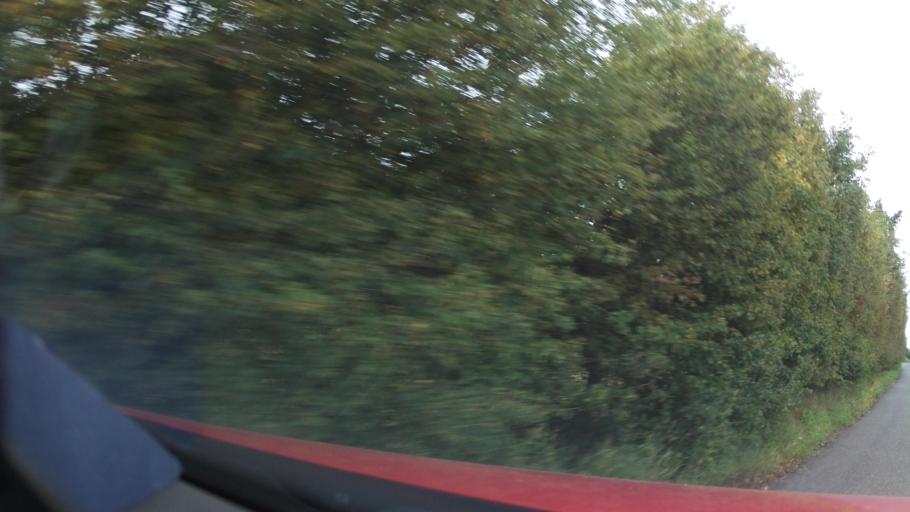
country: GB
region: England
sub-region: Derbyshire
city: Repton
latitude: 52.8116
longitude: -1.5446
